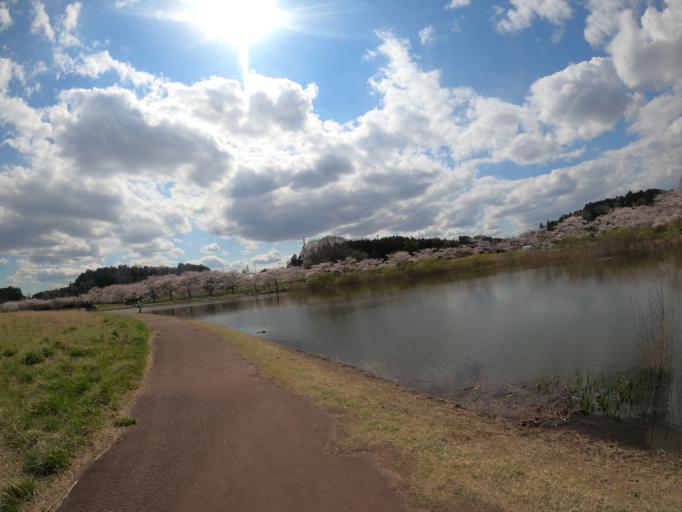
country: JP
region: Miyagi
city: Wakuya
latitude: 38.6202
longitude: 141.2332
